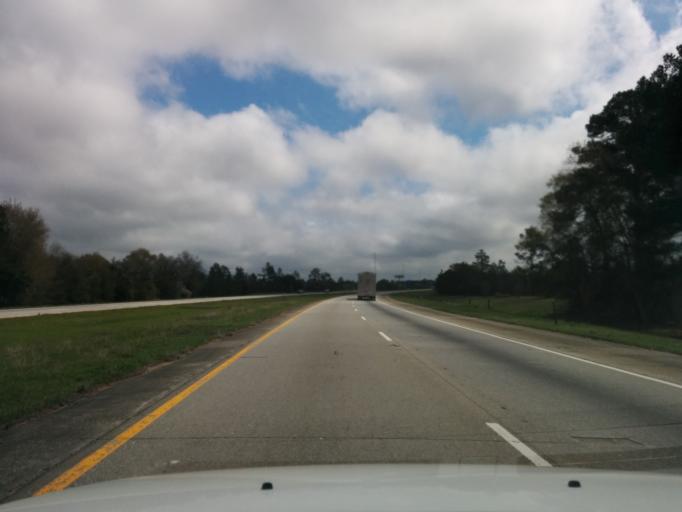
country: US
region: Georgia
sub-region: Emanuel County
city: Swainsboro
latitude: 32.4076
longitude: -82.3196
